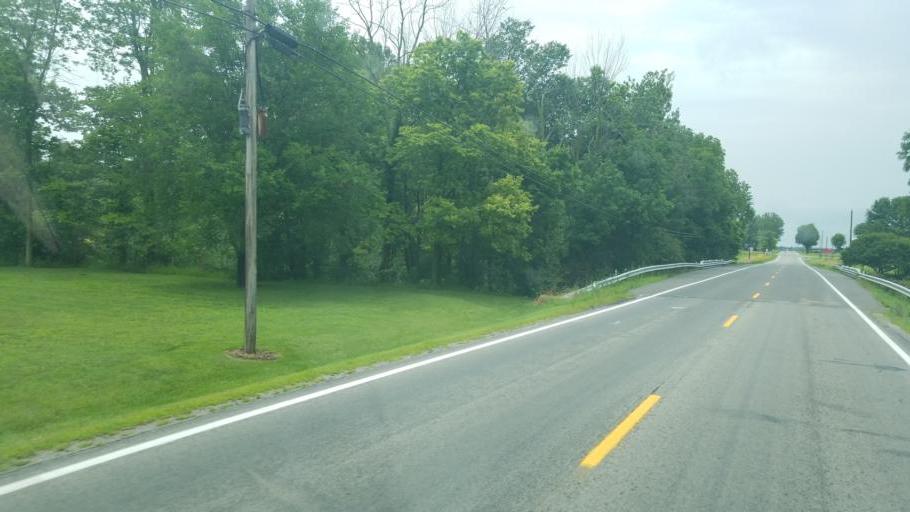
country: US
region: Ohio
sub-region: Hardin County
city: Kenton
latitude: 40.6250
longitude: -83.6484
